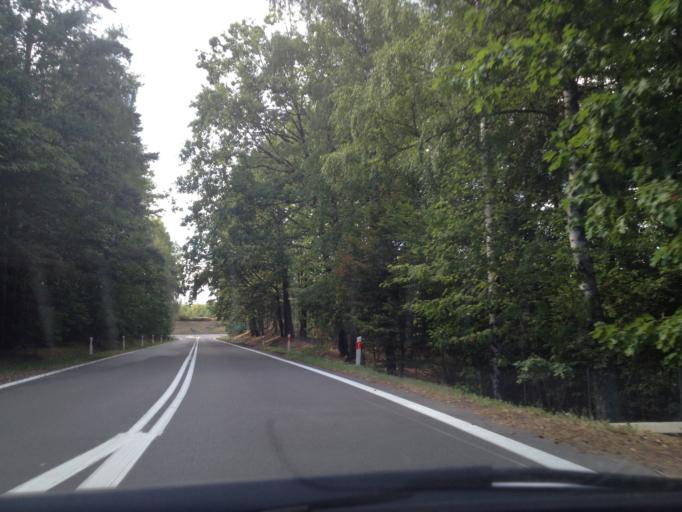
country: PL
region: Lubusz
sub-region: Powiat zaganski
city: Wymiarki
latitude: 51.5647
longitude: 15.0510
